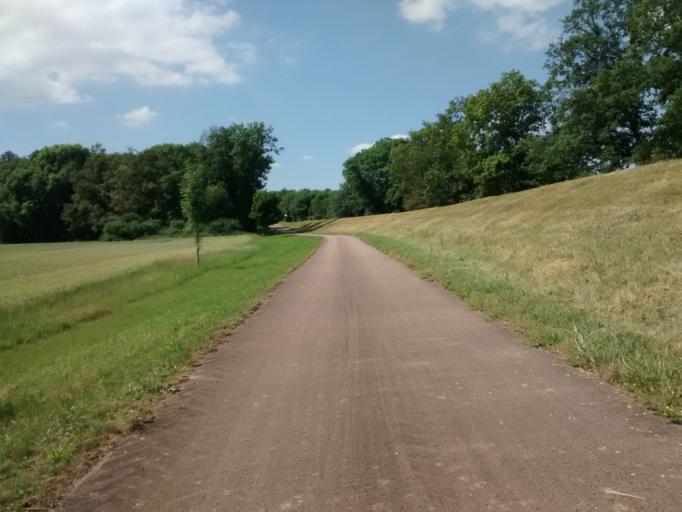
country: DE
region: Saxony-Anhalt
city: Bergwitz
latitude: 51.8478
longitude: 12.5252
